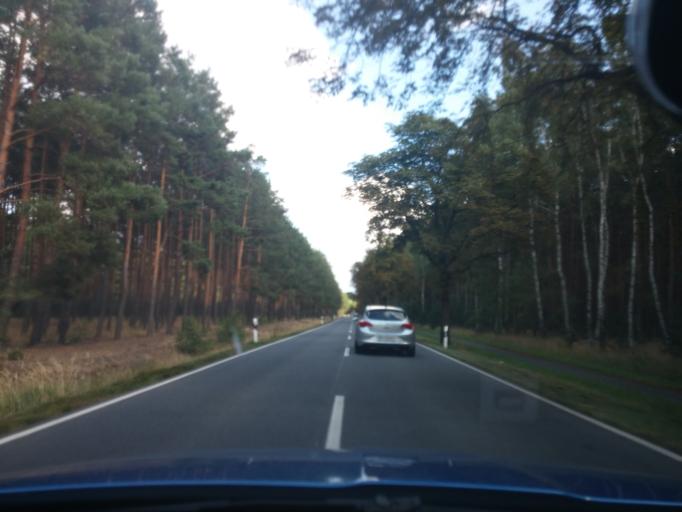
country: DE
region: Brandenburg
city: Halbe
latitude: 52.1071
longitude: 13.7233
